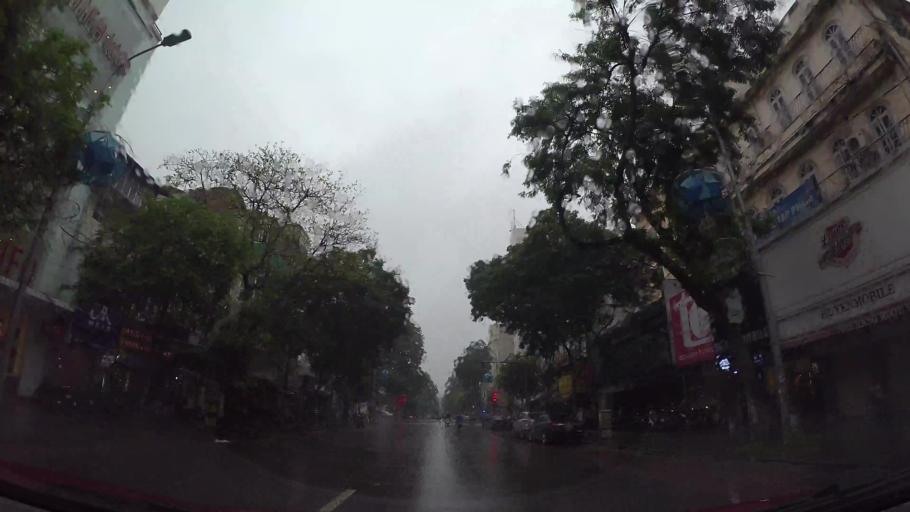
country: VN
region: Ha Noi
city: Hoan Kiem
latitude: 21.0239
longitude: 105.8509
